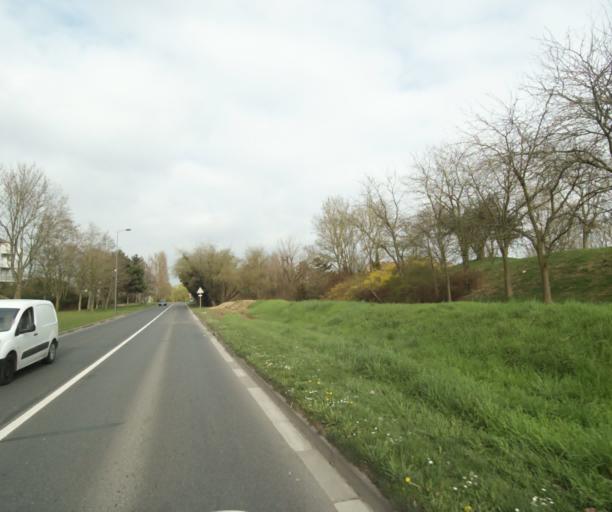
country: FR
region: Ile-de-France
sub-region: Departement du Val-d'Oise
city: Vaureal
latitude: 49.0471
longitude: 2.0421
